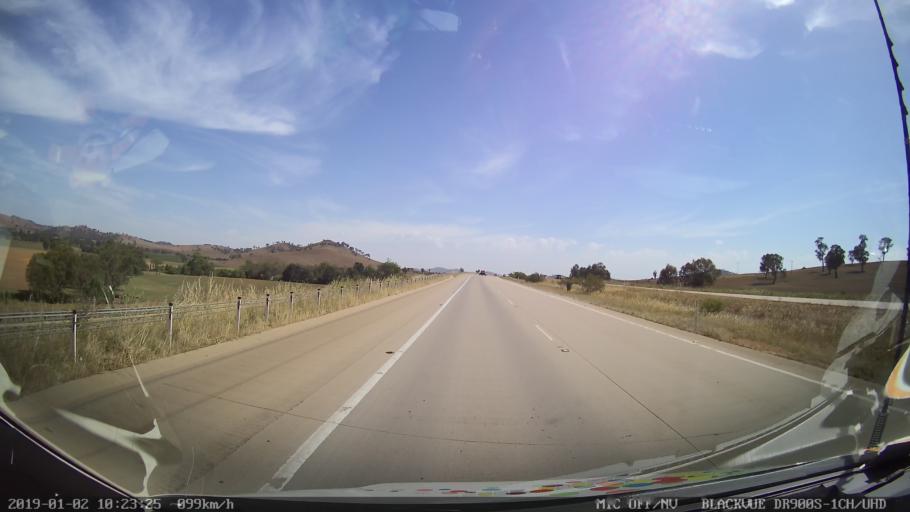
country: AU
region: New South Wales
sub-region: Gundagai
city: Gundagai
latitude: -34.9592
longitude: 148.1567
